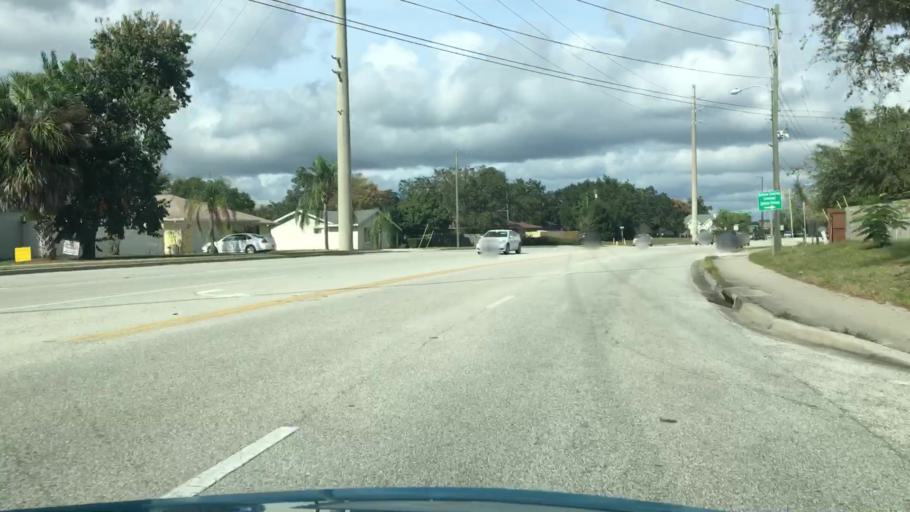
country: US
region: Florida
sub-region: Volusia County
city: Deltona
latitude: 28.9037
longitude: -81.2452
